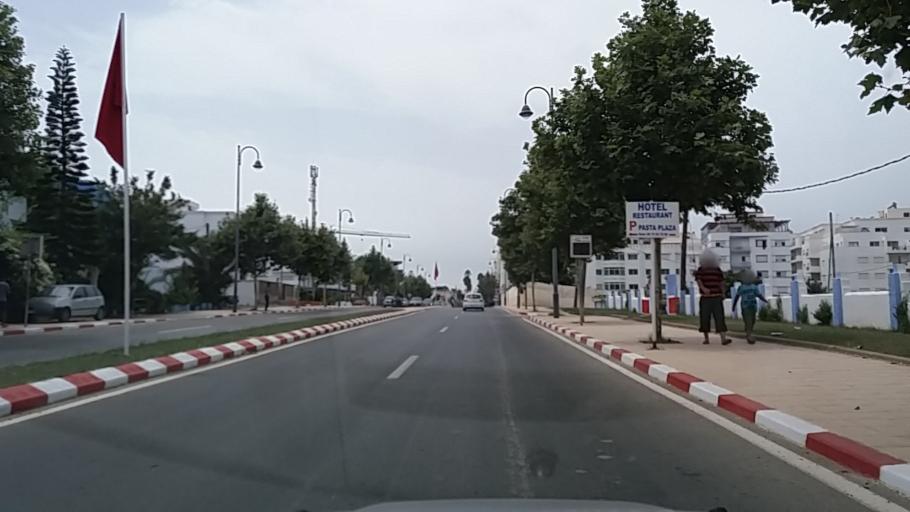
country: MA
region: Tanger-Tetouan
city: Asilah
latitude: 35.4719
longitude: -6.0281
